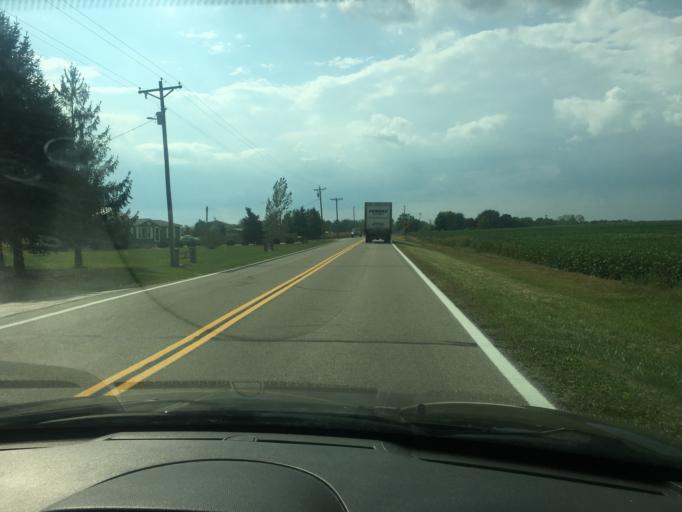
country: US
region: Ohio
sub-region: Champaign County
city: Urbana
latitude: 40.1562
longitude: -83.8304
